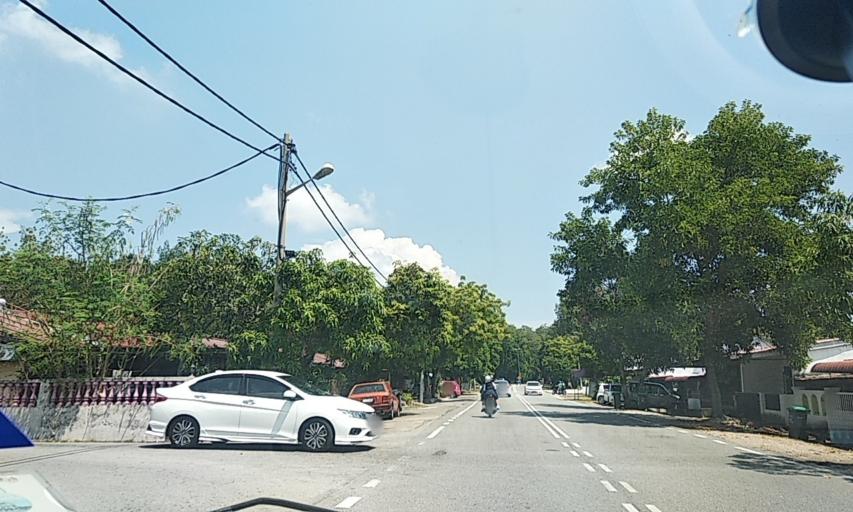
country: MY
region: Kedah
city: Sungai Petani
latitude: 5.6346
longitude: 100.4805
